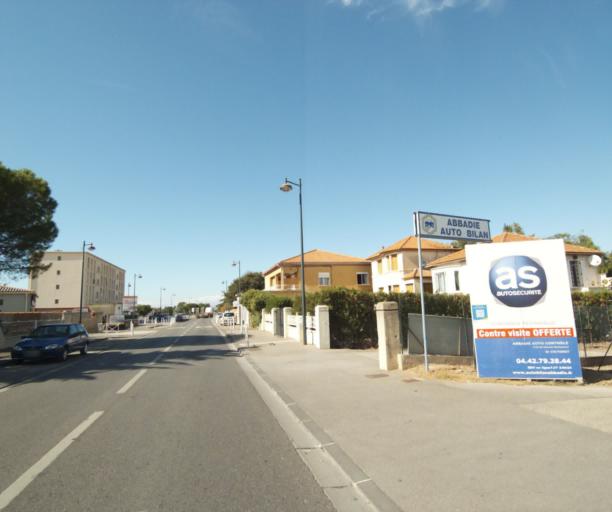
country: FR
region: Provence-Alpes-Cote d'Azur
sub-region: Departement des Bouches-du-Rhone
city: Saint-Victoret
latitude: 43.4144
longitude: 5.2466
